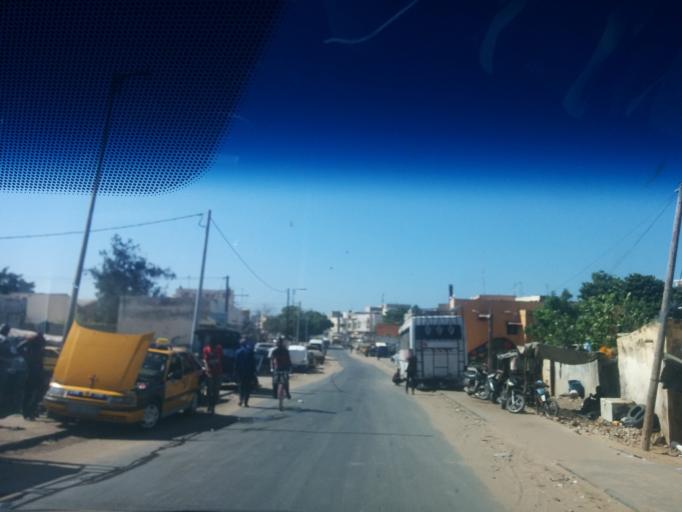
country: SN
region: Dakar
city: Grand Dakar
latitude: 14.7388
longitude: -17.4428
